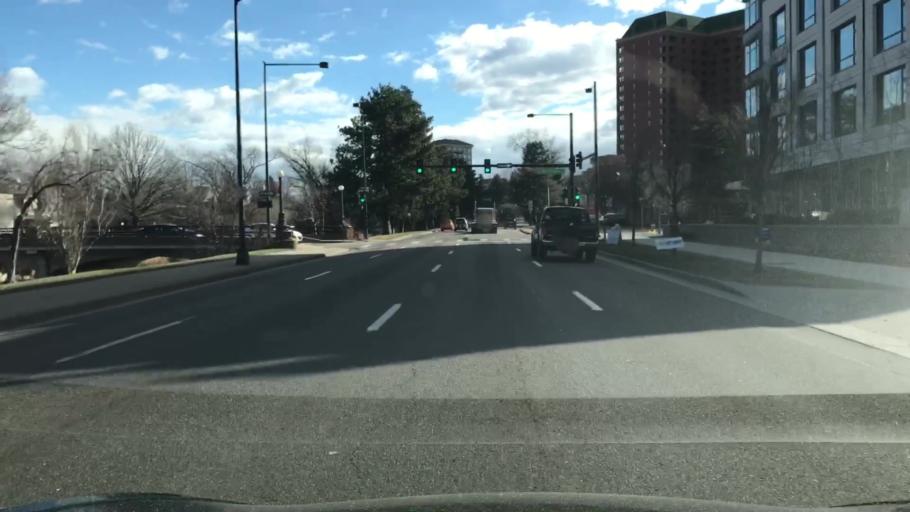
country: US
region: Colorado
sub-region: Denver County
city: Denver
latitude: 39.7208
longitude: -104.9798
